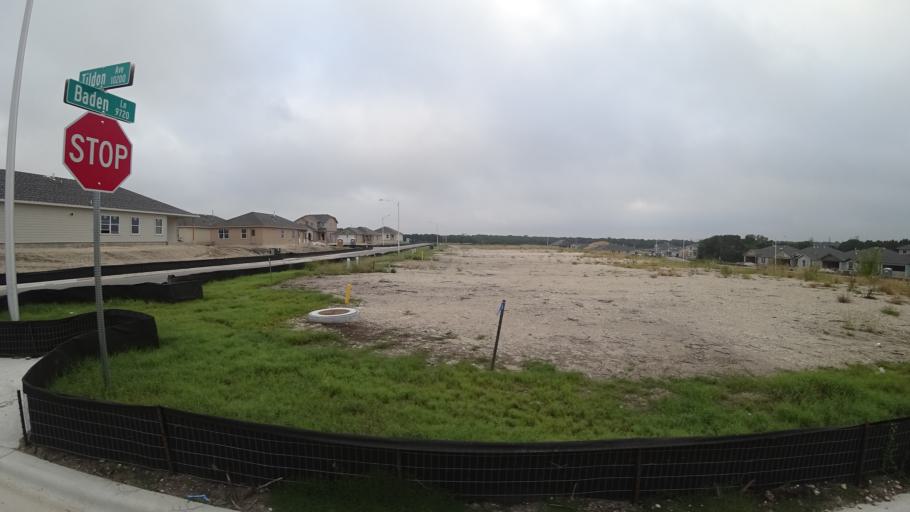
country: US
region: Texas
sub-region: Travis County
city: Wells Branch
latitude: 30.3561
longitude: -97.6632
